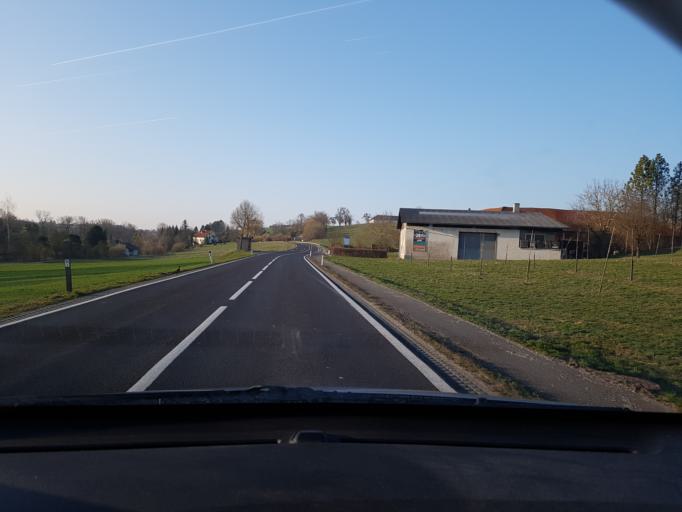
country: AT
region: Upper Austria
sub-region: Politischer Bezirk Linz-Land
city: Ansfelden
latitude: 48.1347
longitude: 14.3308
